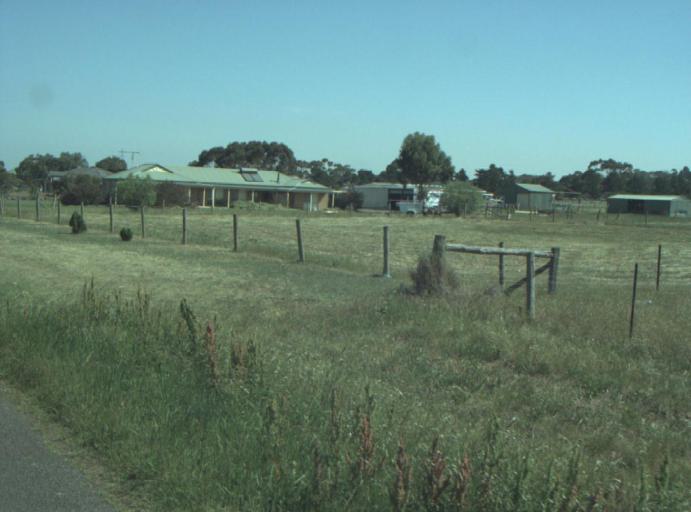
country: AU
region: Victoria
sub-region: Greater Geelong
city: Lara
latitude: -38.0240
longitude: 144.3576
